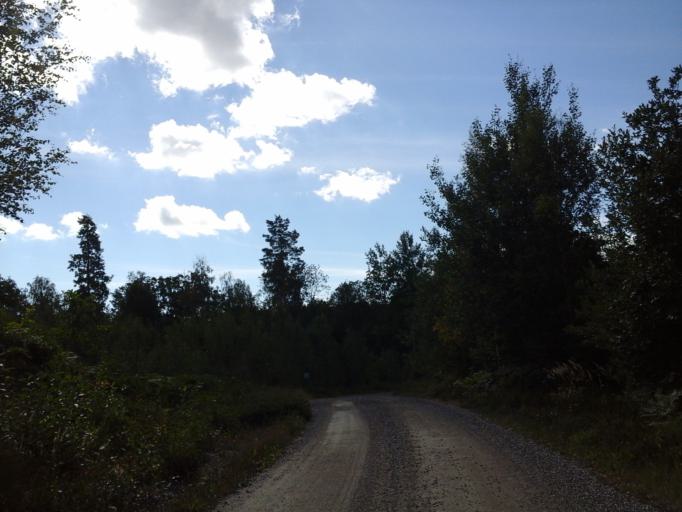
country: SE
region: Soedermanland
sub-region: Eskilstuna Kommun
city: Arla
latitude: 59.2419
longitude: 16.7708
